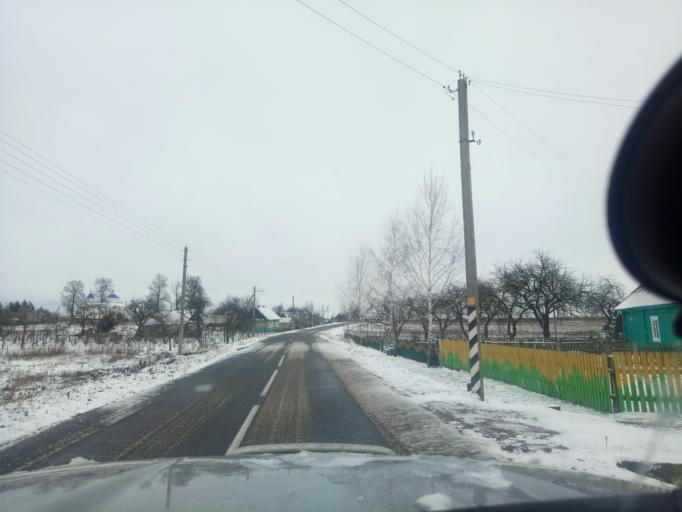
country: BY
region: Minsk
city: Klyetsk
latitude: 53.0235
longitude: 26.7153
